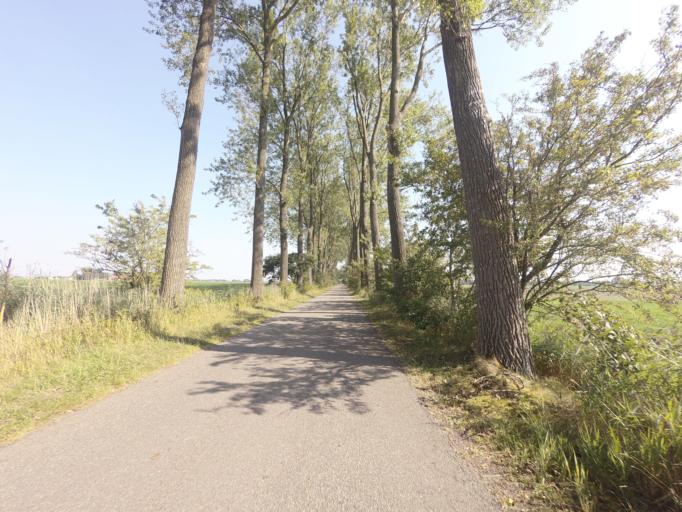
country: NL
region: Groningen
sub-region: Gemeente Zuidhorn
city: Zuidhorn
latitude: 53.2353
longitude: 6.4188
